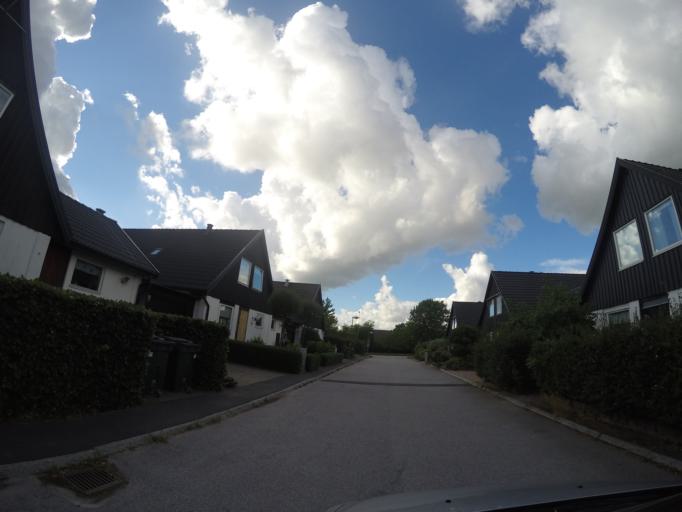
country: SE
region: Skane
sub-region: Lunds Kommun
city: Lund
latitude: 55.6989
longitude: 13.2390
